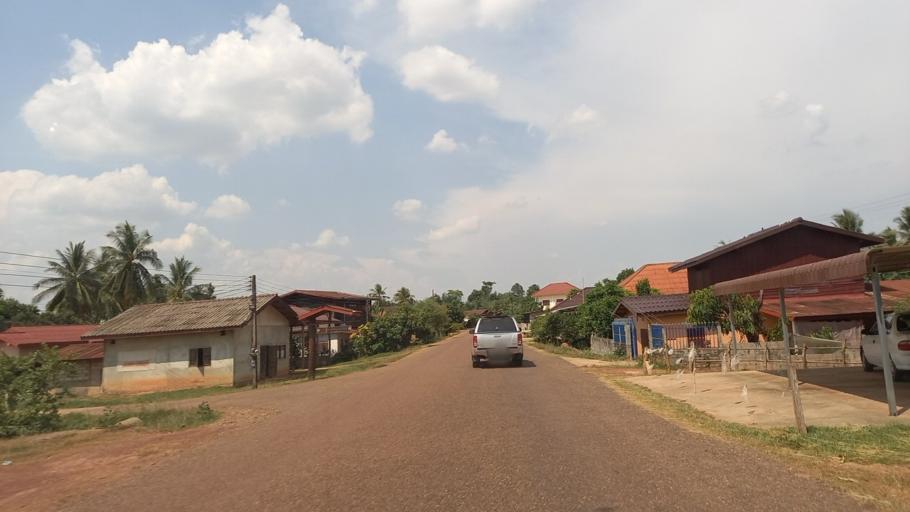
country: LA
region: Bolikhamxai
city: Muang Pakxan
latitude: 18.4272
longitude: 103.7108
